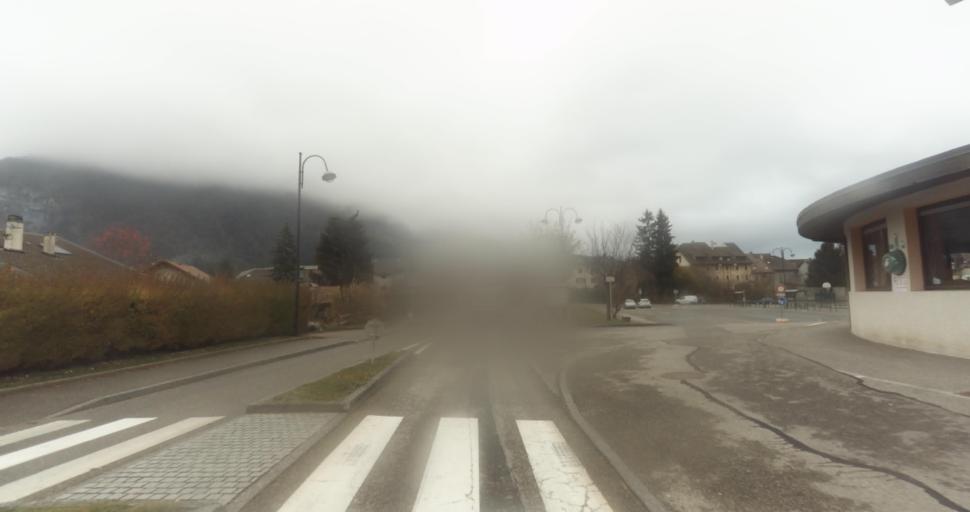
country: FR
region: Rhone-Alpes
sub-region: Departement de la Haute-Savoie
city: Thorens-Glieres
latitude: 45.9977
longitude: 6.2501
